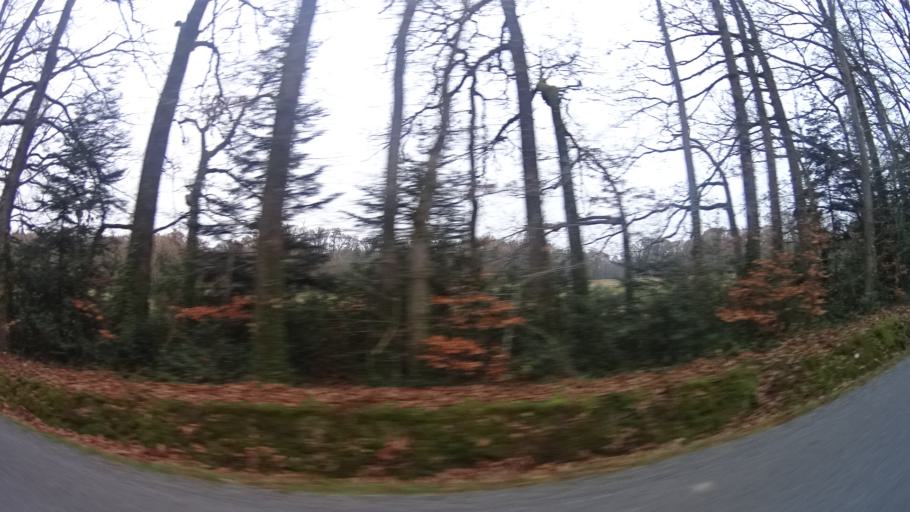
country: FR
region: Brittany
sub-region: Departement d'Ille-et-Vilaine
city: Bains-sur-Oust
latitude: 47.7066
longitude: -2.0472
